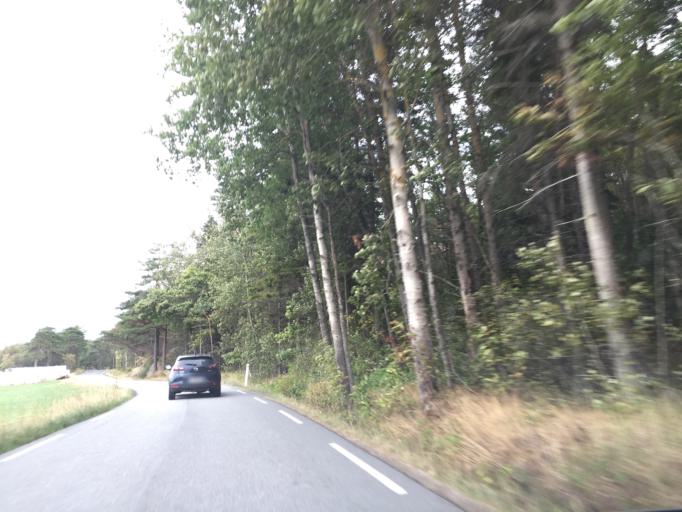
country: NO
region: Ostfold
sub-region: Hvaler
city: Skjaerhalden
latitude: 59.0356
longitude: 11.0265
